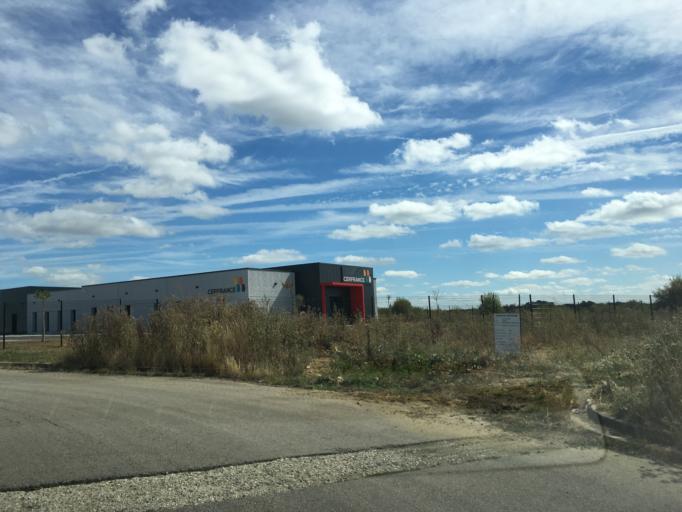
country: FR
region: Haute-Normandie
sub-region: Departement de l'Eure
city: Saint-Marcel
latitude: 49.0648
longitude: 1.4261
